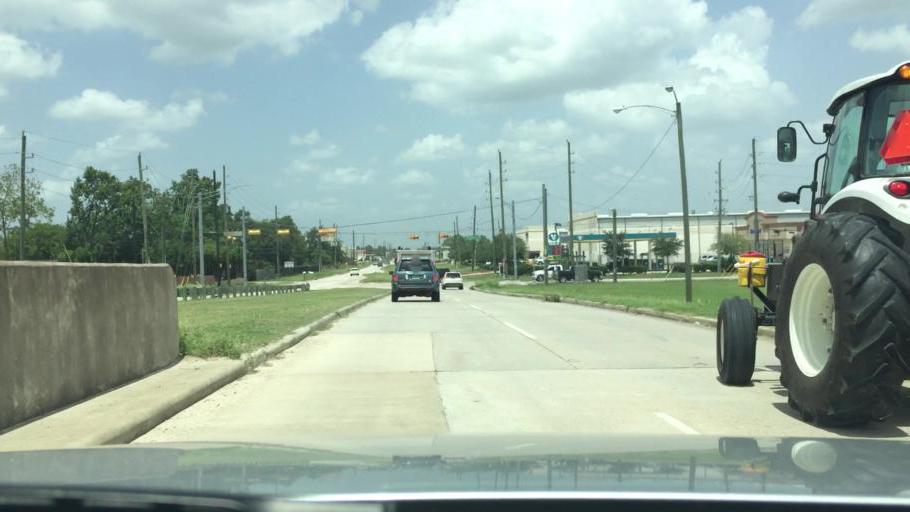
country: US
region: Texas
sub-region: Harris County
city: Hudson
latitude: 29.9495
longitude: -95.5199
